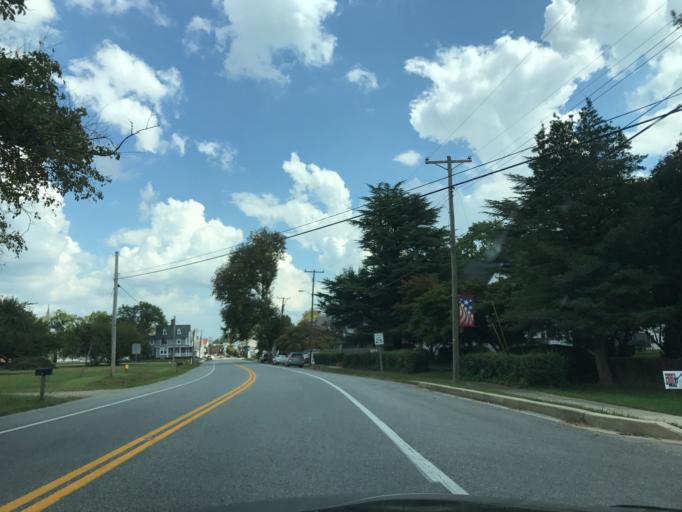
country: US
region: Maryland
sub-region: Queen Anne's County
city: Kingstown
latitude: 39.1864
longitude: -75.8619
